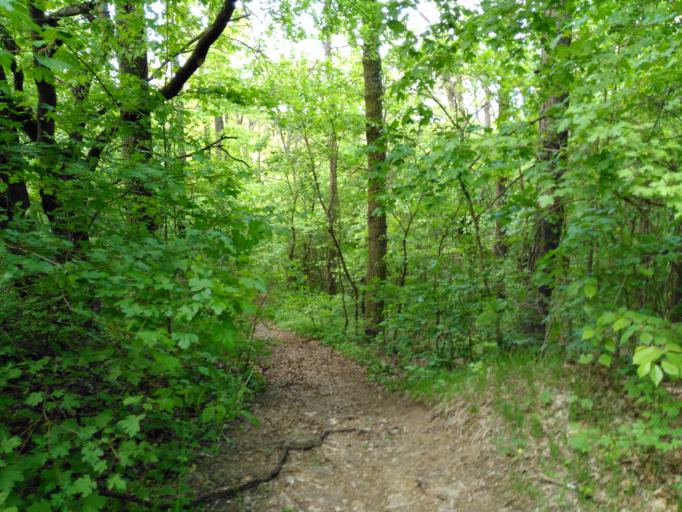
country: CZ
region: Central Bohemia
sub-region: Okres Beroun
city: Kraluv Dvur
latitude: 49.9183
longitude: 14.0664
